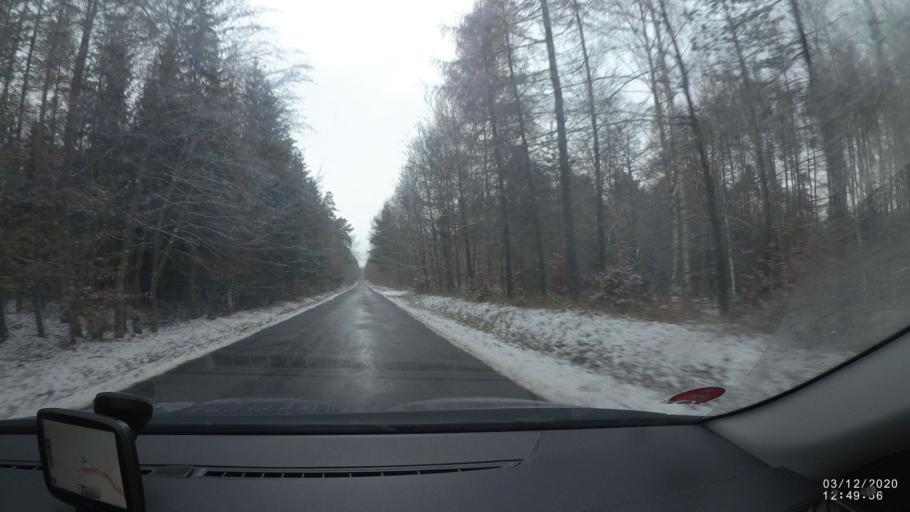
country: CZ
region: Central Bohemia
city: Nove Straseci
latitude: 50.1678
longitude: 13.8688
